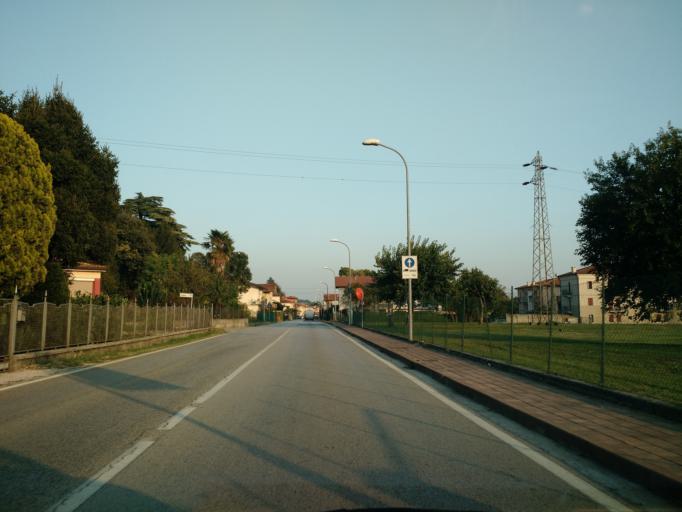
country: IT
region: Veneto
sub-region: Provincia di Vicenza
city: Breganze
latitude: 45.7076
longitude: 11.5553
